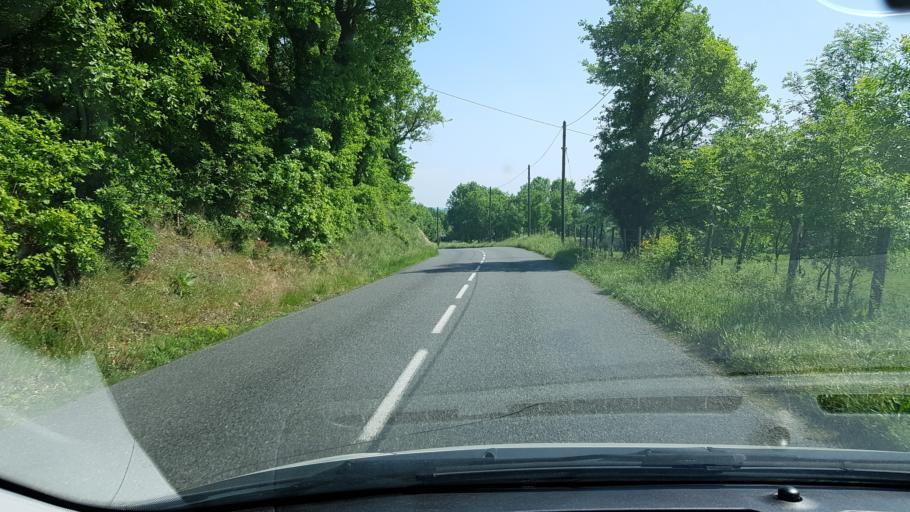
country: FR
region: Rhone-Alpes
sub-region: Departement du Rhone
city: Brignais
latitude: 45.6550
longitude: 4.7435
